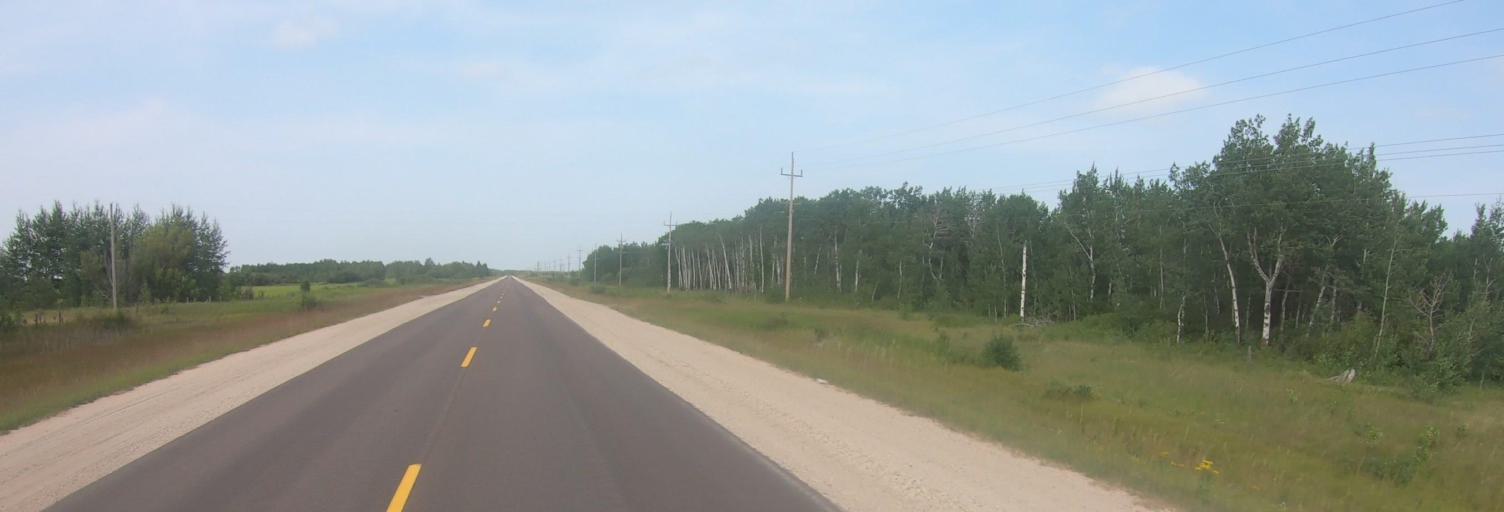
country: CA
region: Manitoba
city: La Broquerie
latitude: 49.2669
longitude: -96.4533
